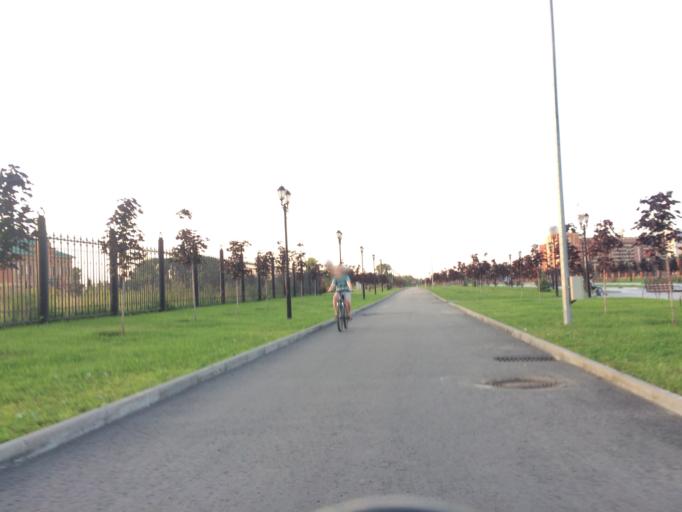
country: RU
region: Mariy-El
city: Yoshkar-Ola
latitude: 56.6387
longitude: 47.9129
